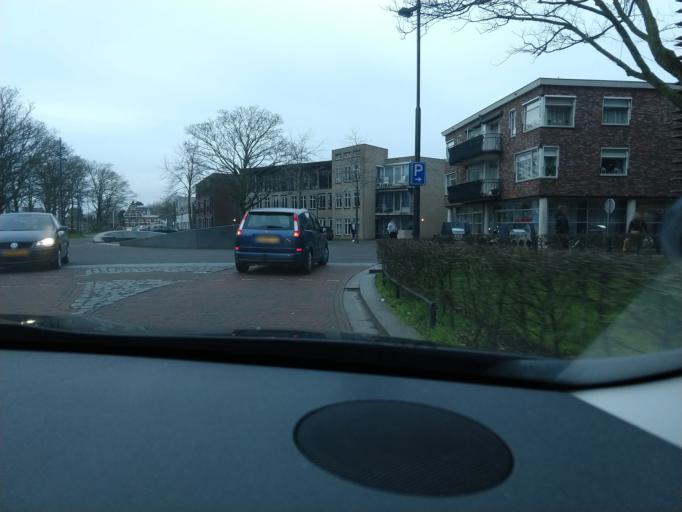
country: NL
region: Zeeland
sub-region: Gemeente Middelburg
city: Middelburg
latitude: 51.4652
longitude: 3.6042
